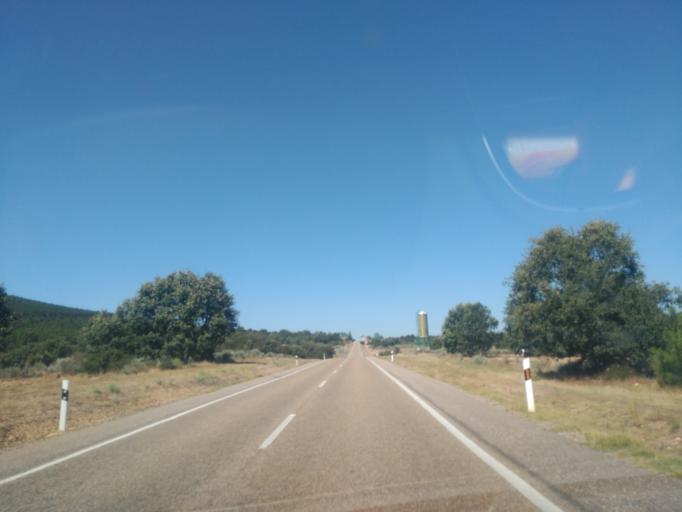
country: ES
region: Castille and Leon
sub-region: Provincia de Zamora
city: Otero de Bodas
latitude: 41.9357
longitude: -6.1364
